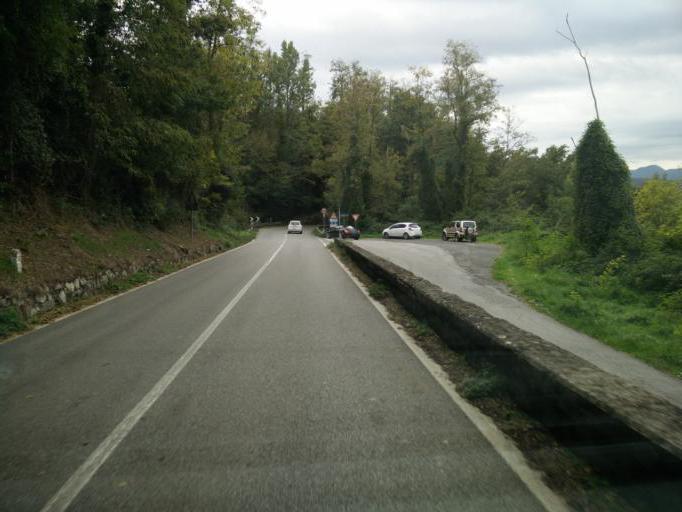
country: IT
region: Tuscany
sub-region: Provincia di Massa-Carrara
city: Fivizzano
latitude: 44.2171
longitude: 10.0933
